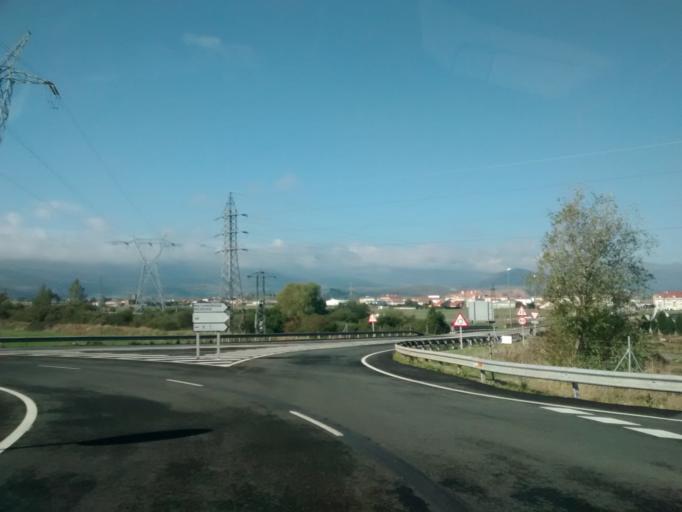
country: ES
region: Cantabria
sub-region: Provincia de Cantabria
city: Reinosa
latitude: 42.9856
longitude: -4.1352
